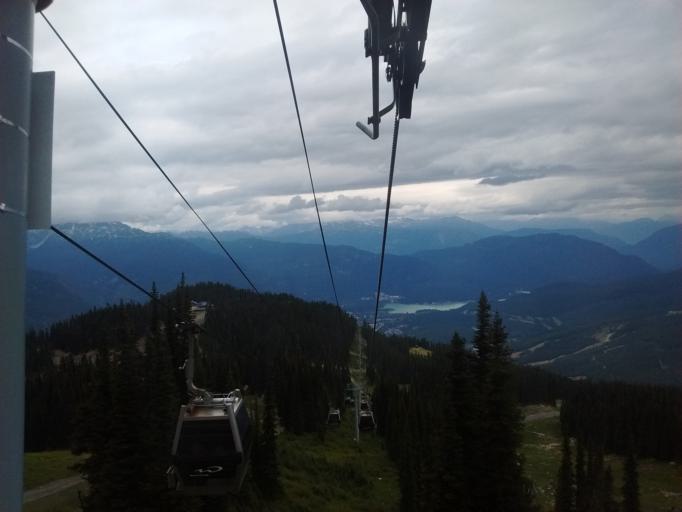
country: CA
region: British Columbia
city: Whistler
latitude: 50.0728
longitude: -122.9475
